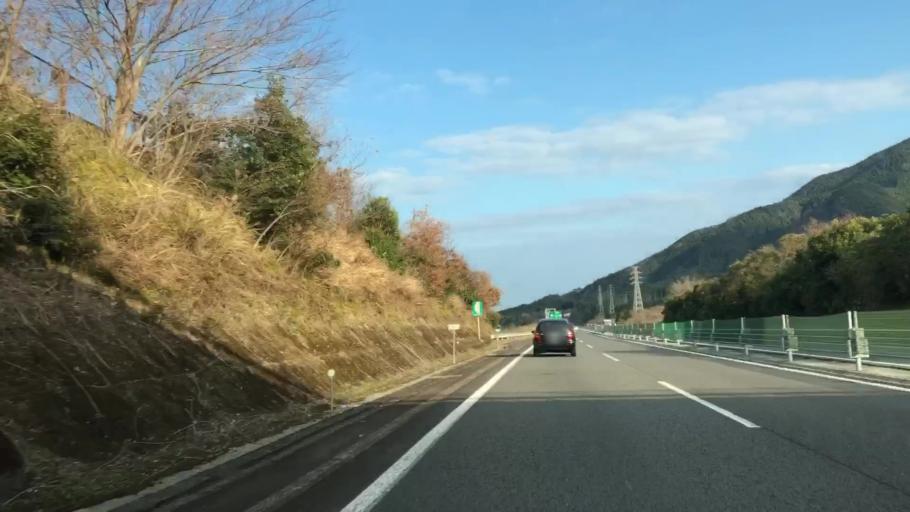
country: JP
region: Miyazaki
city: Miyazaki-shi
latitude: 31.8327
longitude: 131.3258
